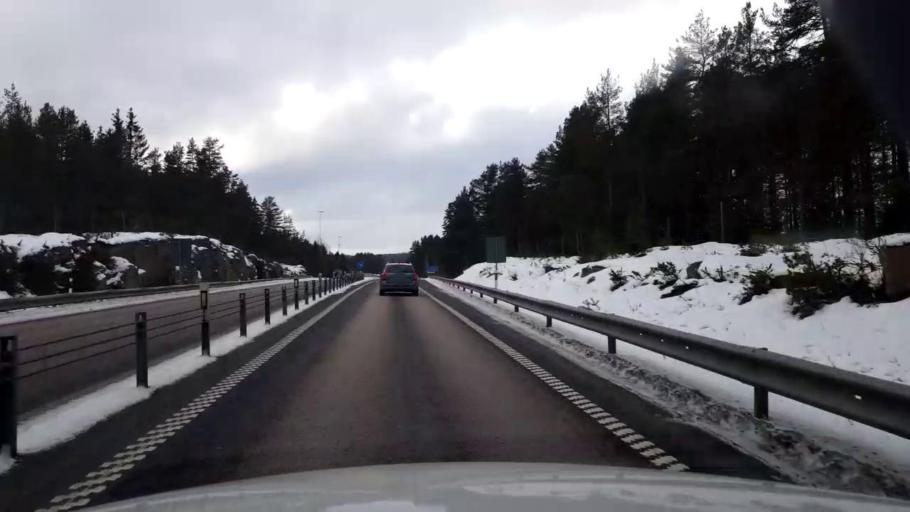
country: SE
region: Gaevleborg
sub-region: Hudiksvalls Kommun
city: Hudiksvall
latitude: 61.8057
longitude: 17.1795
